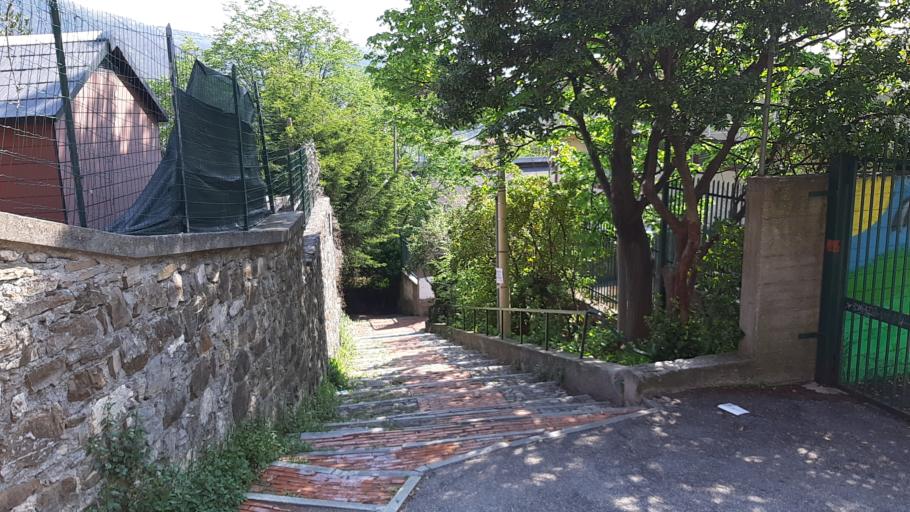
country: IT
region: Liguria
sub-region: Provincia di Genova
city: Bogliasco
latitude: 44.4321
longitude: 9.0184
